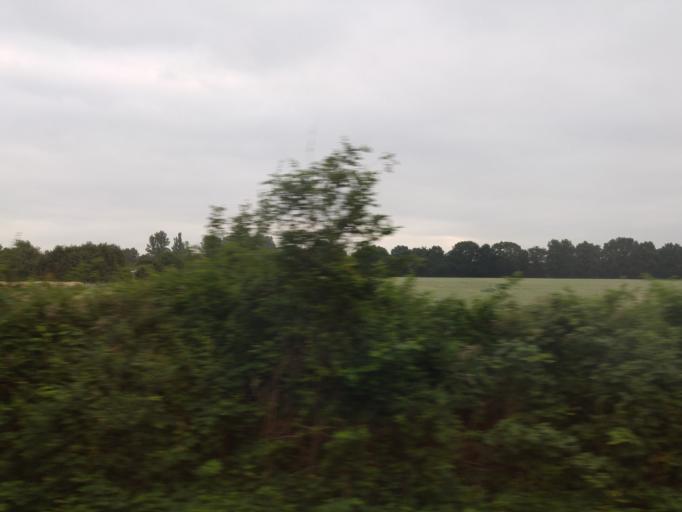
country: DE
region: Hesse
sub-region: Regierungsbezirk Darmstadt
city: Erzhausen
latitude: 49.9595
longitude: 8.6524
